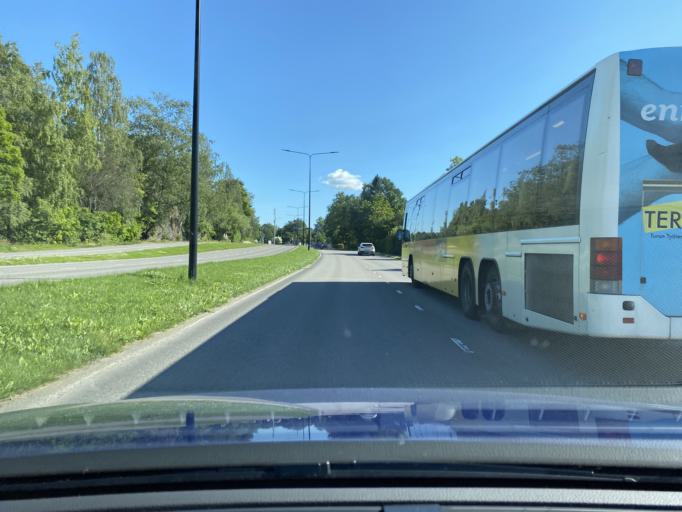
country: FI
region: Varsinais-Suomi
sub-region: Turku
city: Turku
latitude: 60.4665
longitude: 22.2688
